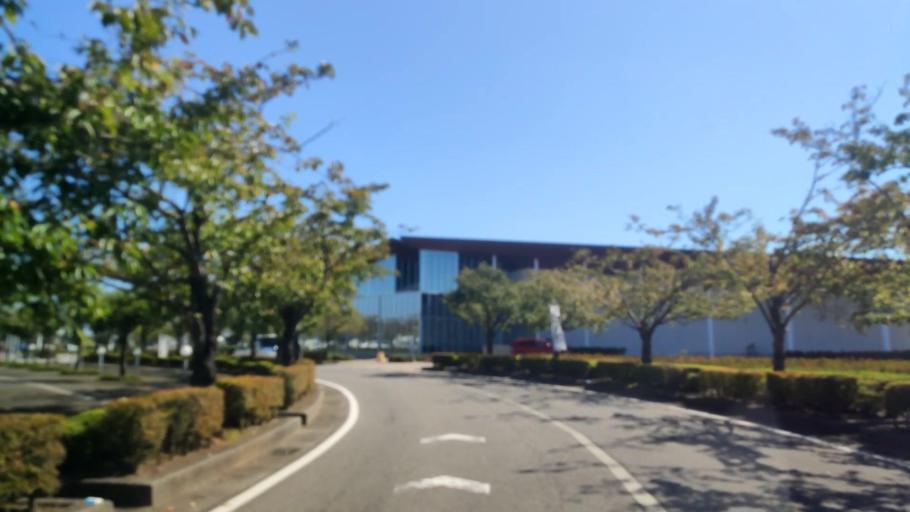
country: JP
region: Ishikawa
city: Nanao
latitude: 37.4436
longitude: 137.2696
